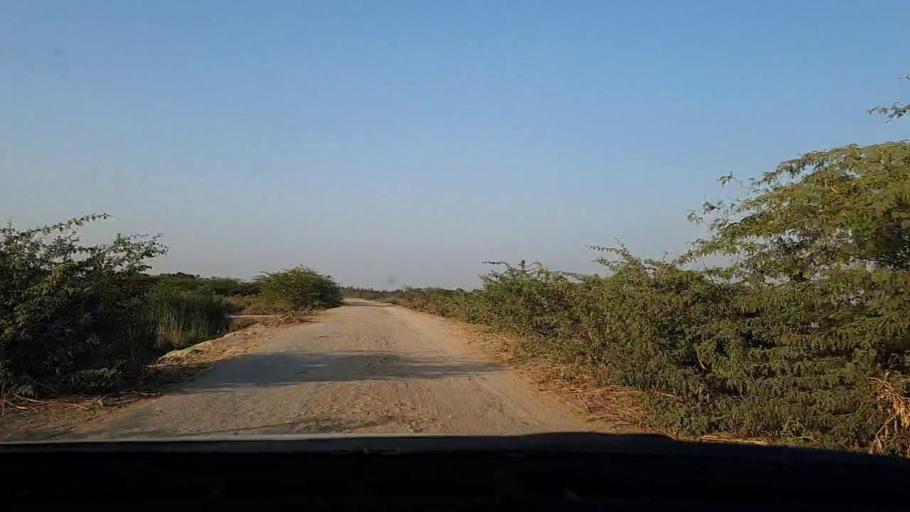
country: PK
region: Sindh
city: Tando Mittha Khan
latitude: 25.8635
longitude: 69.2726
